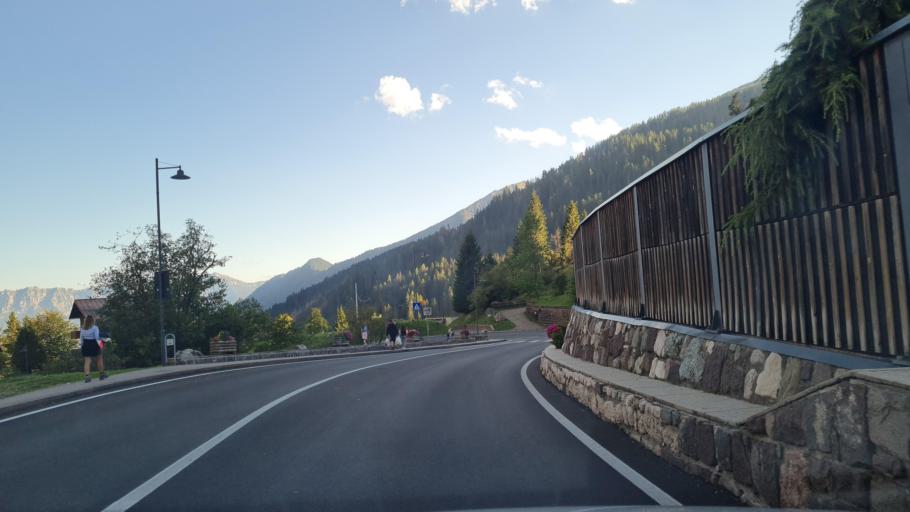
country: IT
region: Trentino-Alto Adige
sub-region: Provincia di Trento
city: Siror
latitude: 46.2577
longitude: 11.8025
